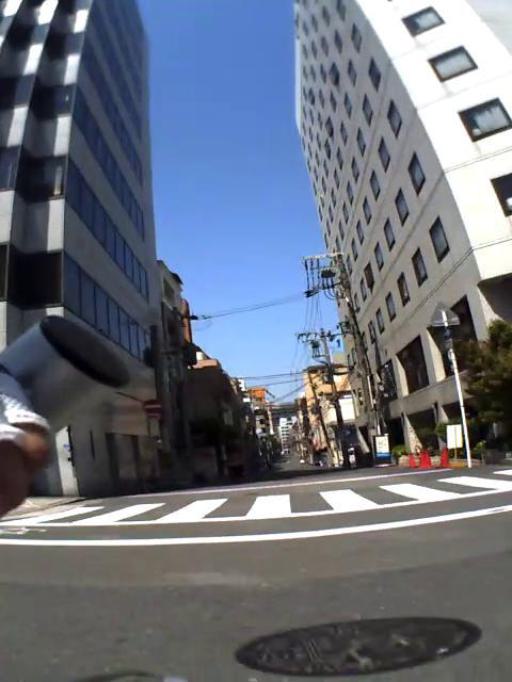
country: JP
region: Osaka
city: Osaka-shi
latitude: 34.6842
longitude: 135.5174
